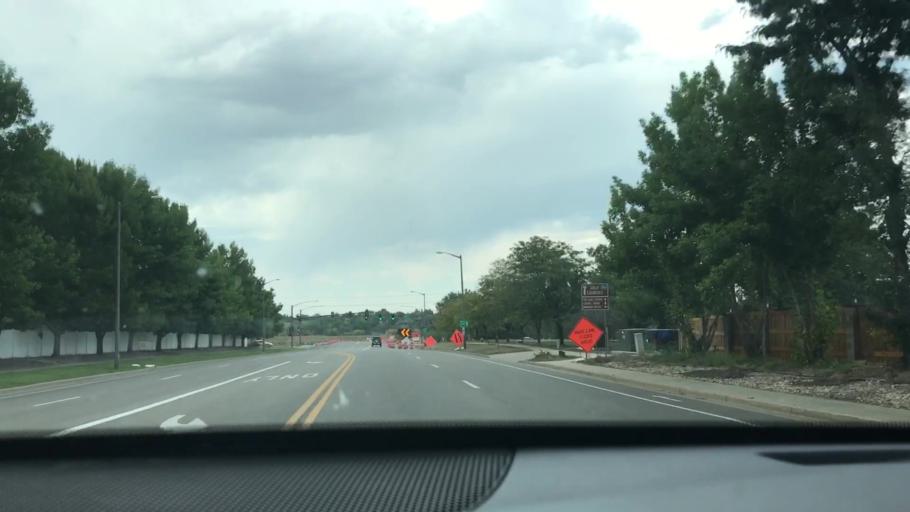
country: US
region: Colorado
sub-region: Larimer County
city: Loveland
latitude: 40.3909
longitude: -105.1159
